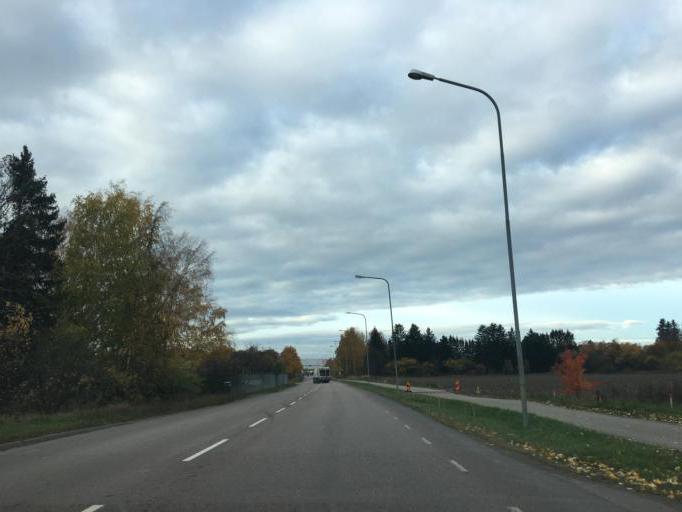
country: SE
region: Vaestmanland
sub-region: Vasteras
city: Vasteras
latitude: 59.5898
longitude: 16.4941
